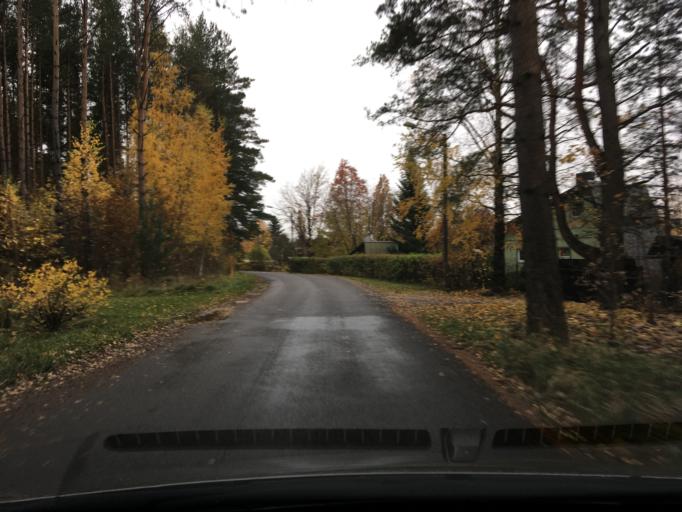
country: EE
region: Tartu
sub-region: Tartu linn
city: Tartu
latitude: 58.3525
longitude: 26.7797
